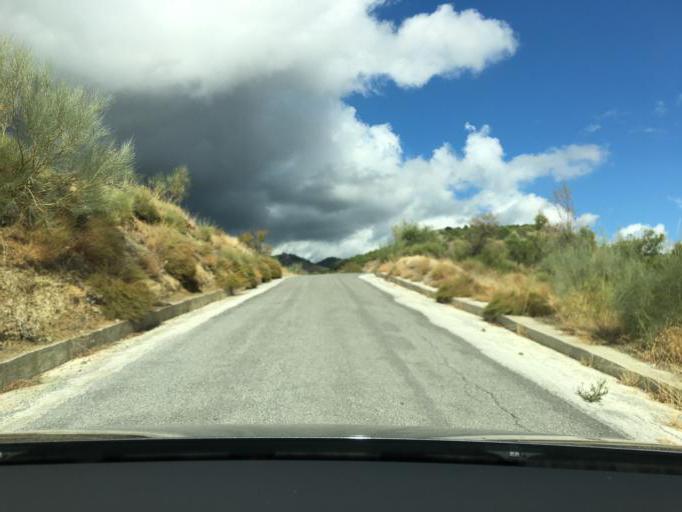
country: ES
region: Andalusia
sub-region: Provincia de Granada
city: Quentar
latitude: 37.2062
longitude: -3.4675
